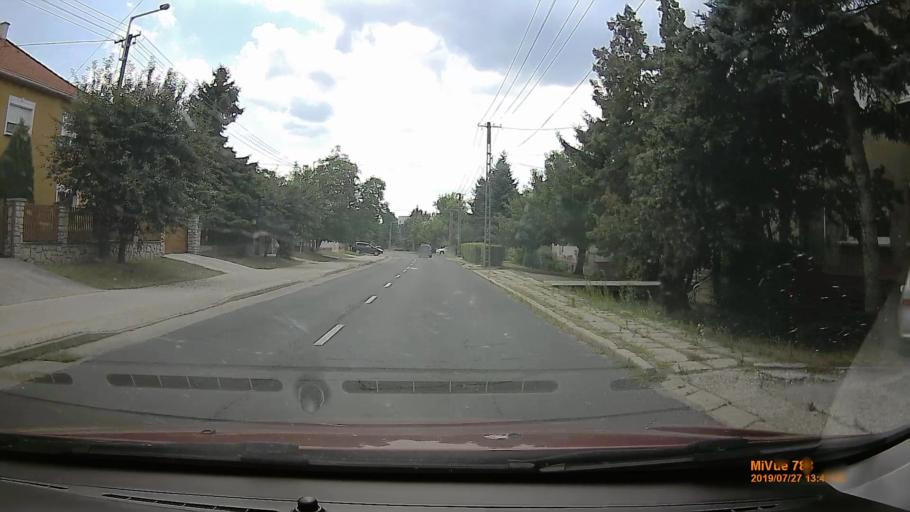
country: HU
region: Veszprem
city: Ajka
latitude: 47.1172
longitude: 17.5640
